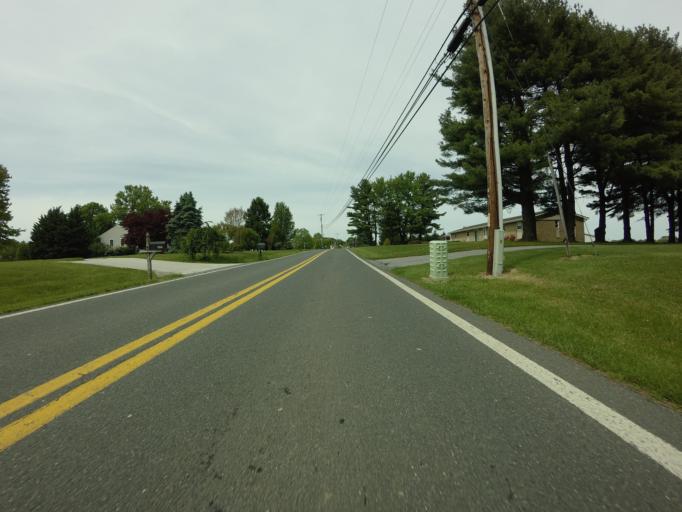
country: US
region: Maryland
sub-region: Carroll County
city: Eldersburg
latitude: 39.4693
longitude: -76.9531
